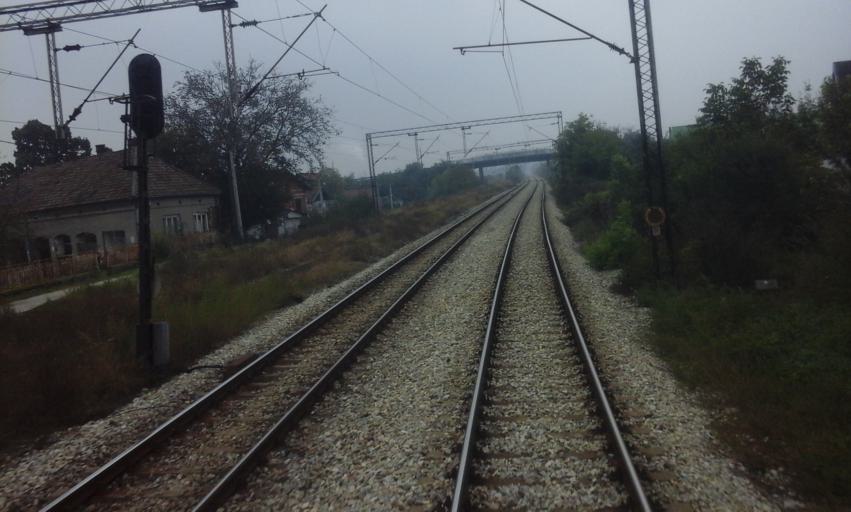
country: RS
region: Central Serbia
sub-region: Sumadijski Okrug
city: Lapovo
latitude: 44.1831
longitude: 21.1029
